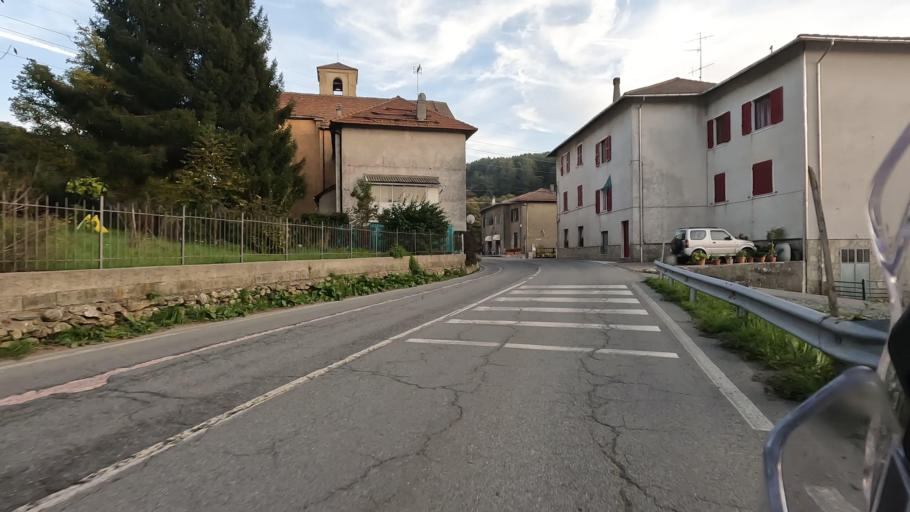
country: IT
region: Liguria
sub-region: Provincia di Savona
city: Osteria dei Cacciatori-Stella
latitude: 44.4308
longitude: 8.4585
